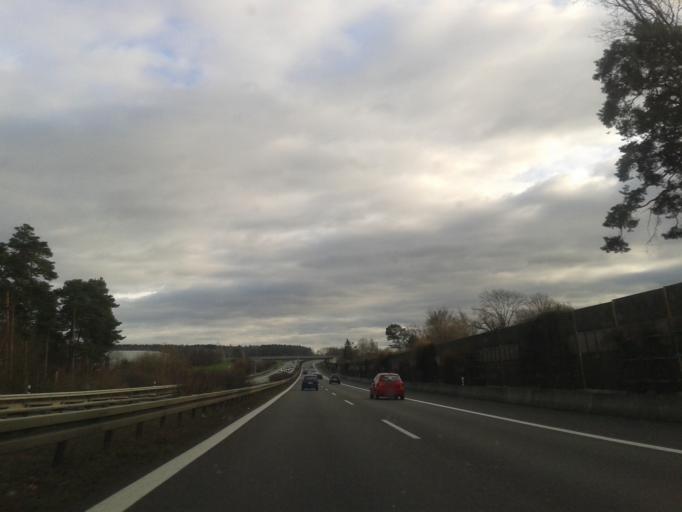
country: DE
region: Saxony
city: Wachau
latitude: 51.1706
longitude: 13.9024
